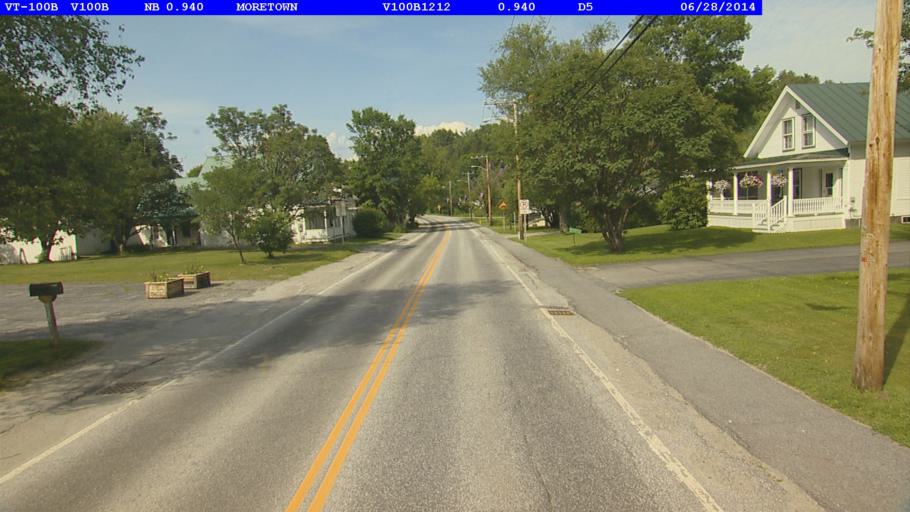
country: US
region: Vermont
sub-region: Washington County
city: Waterbury
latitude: 44.2481
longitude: -72.7631
